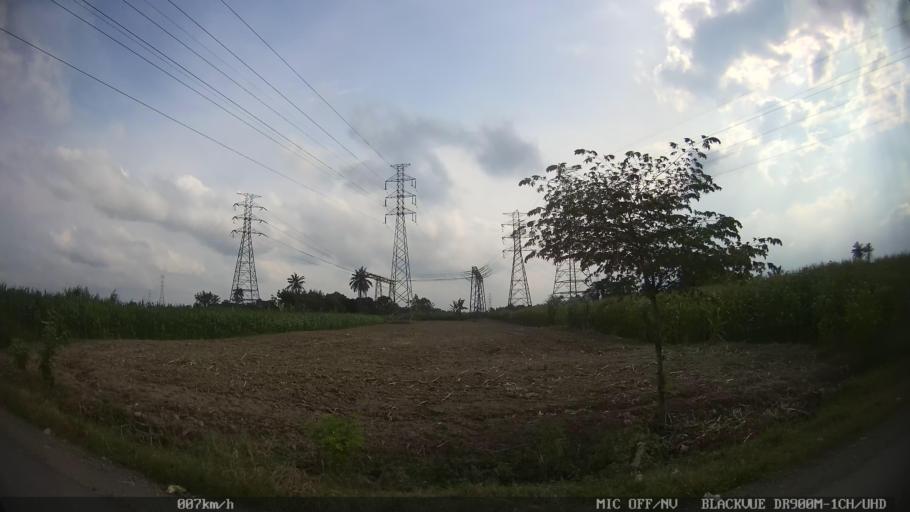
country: ID
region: North Sumatra
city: Percut
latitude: 3.5676
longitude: 98.7829
